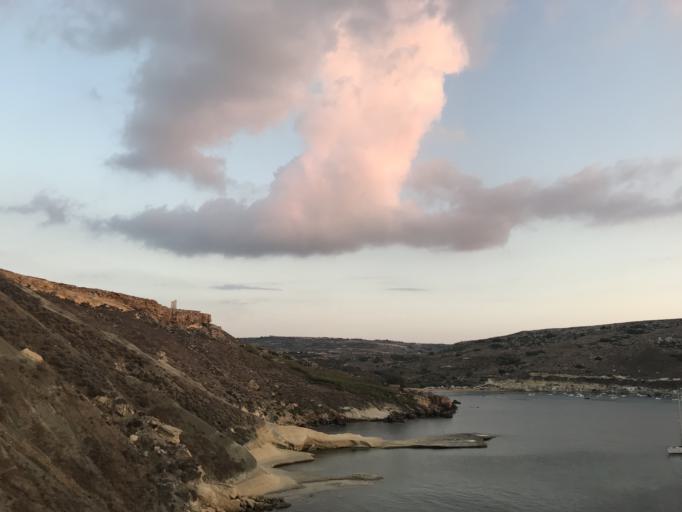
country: MT
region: L-Imgarr
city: Imgarr
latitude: 35.9275
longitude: 14.3433
